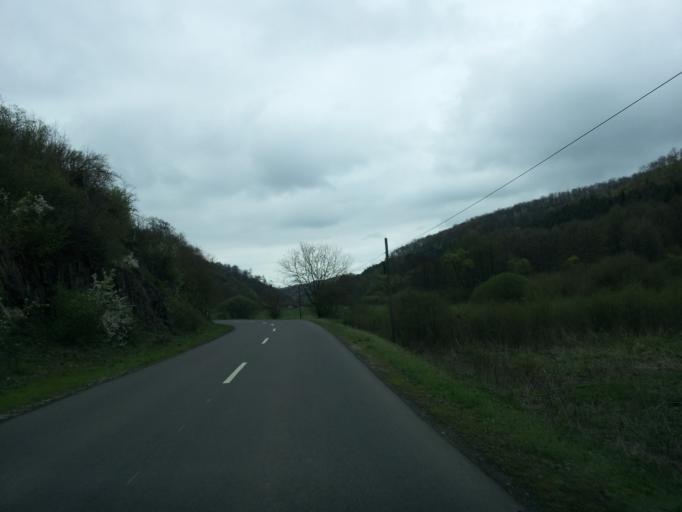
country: HU
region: Borsod-Abauj-Zemplen
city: Rudabanya
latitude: 48.4785
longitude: 20.5742
